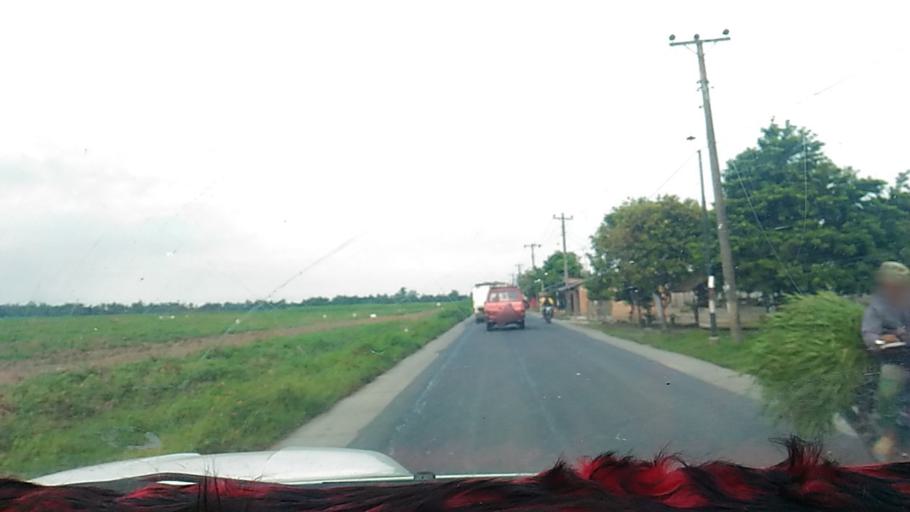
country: ID
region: North Sumatra
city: Labuhan Deli
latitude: 3.7037
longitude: 98.5689
